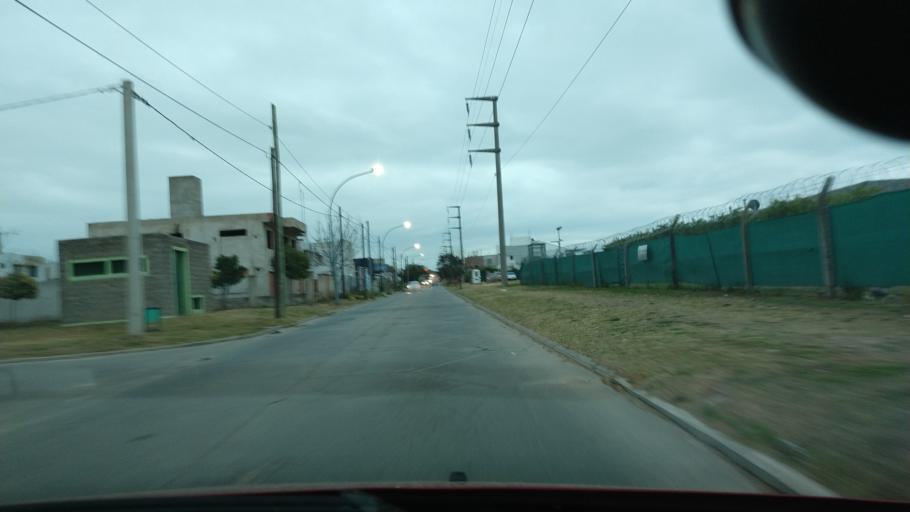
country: AR
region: Cordoba
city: La Calera
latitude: -31.3785
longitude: -64.2673
